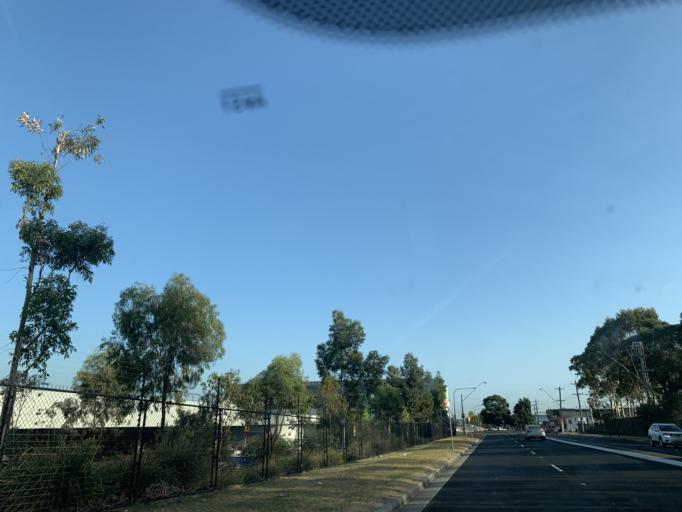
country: AU
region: New South Wales
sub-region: Blacktown
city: Doonside
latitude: -33.7977
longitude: 150.8706
